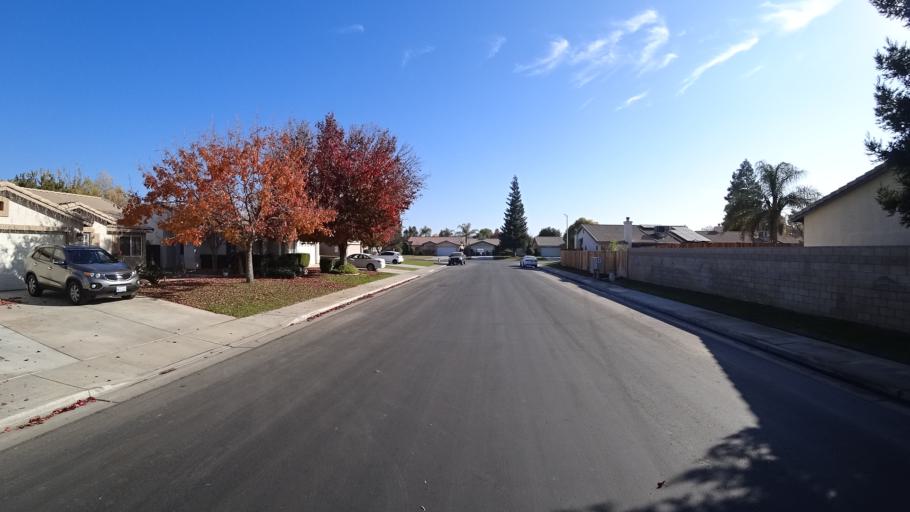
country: US
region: California
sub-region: Kern County
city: Greenfield
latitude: 35.2979
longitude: -119.0653
